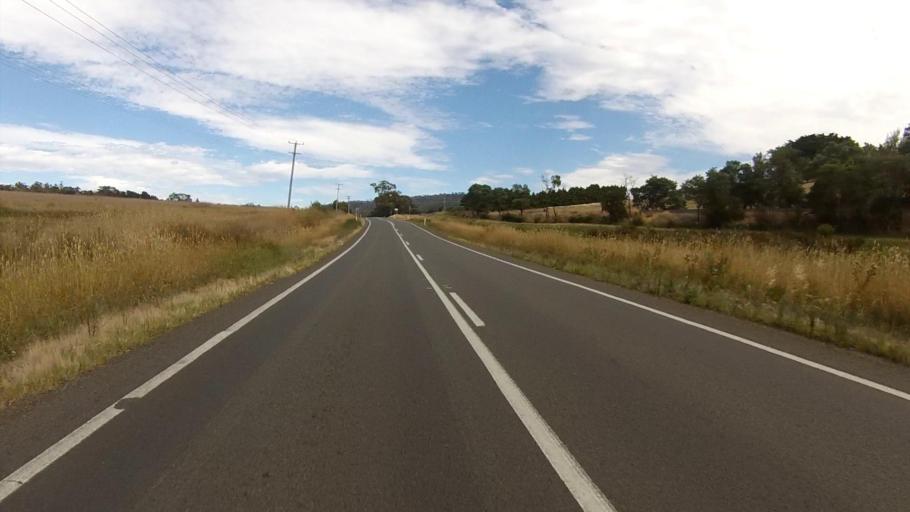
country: AU
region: Tasmania
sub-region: Brighton
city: Old Beach
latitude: -42.6717
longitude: 147.3924
